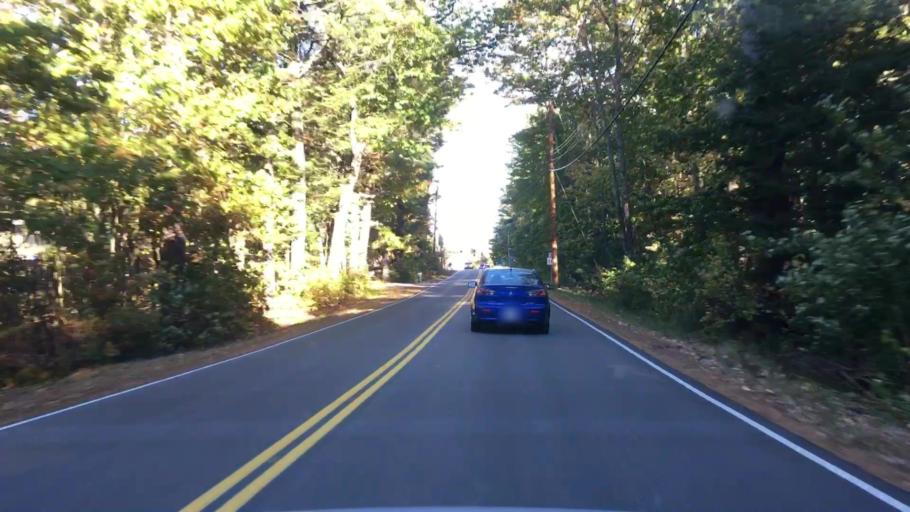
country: US
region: Maine
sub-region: Cumberland County
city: South Portland Gardens
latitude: 43.6182
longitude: -70.3488
